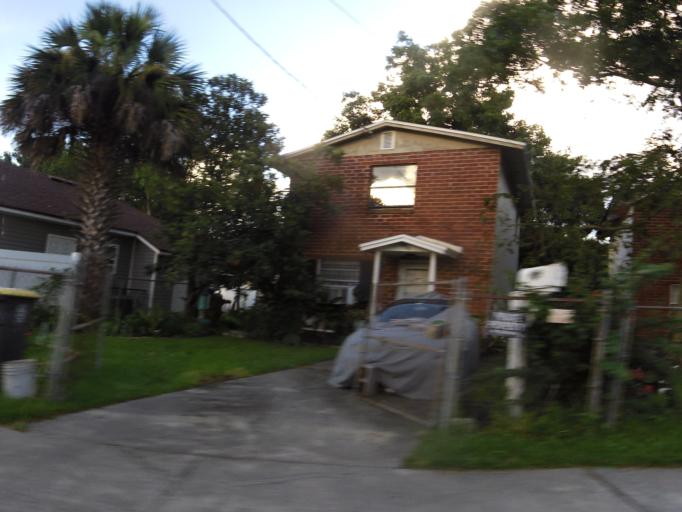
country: US
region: Florida
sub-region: Duval County
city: Jacksonville
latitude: 30.3377
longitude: -81.6852
